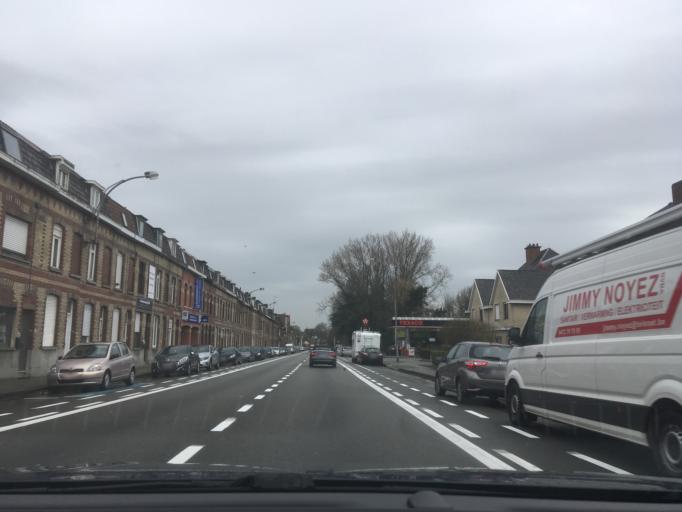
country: BE
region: Flanders
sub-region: Provincie West-Vlaanderen
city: Kortrijk
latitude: 50.8136
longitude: 3.2736
